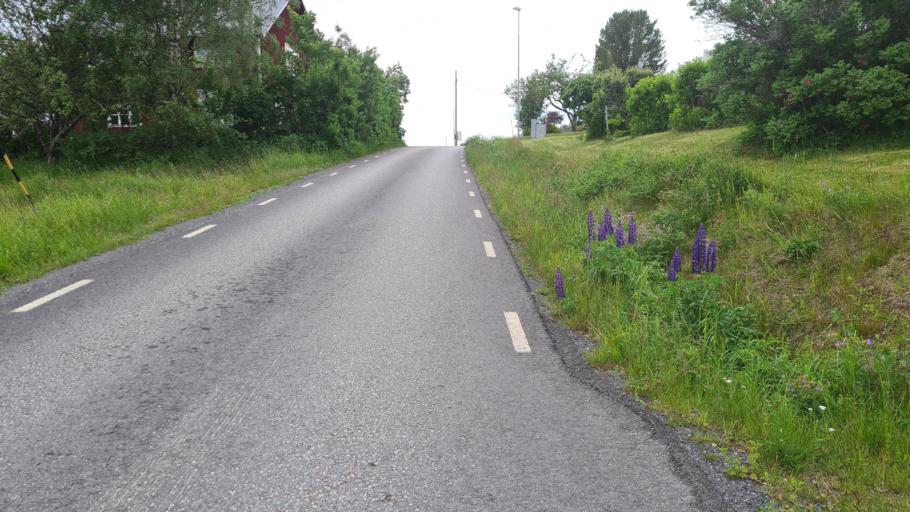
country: SE
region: Vaesternorrland
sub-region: Kramfors Kommun
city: Nordingra
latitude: 62.9795
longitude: 18.4294
